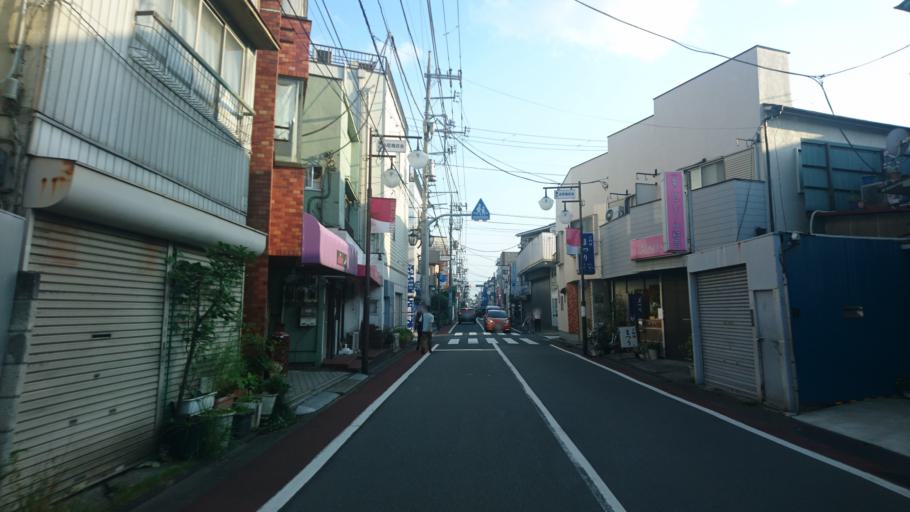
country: JP
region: Kanagawa
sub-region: Kawasaki-shi
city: Kawasaki
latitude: 35.5564
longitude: 139.7171
